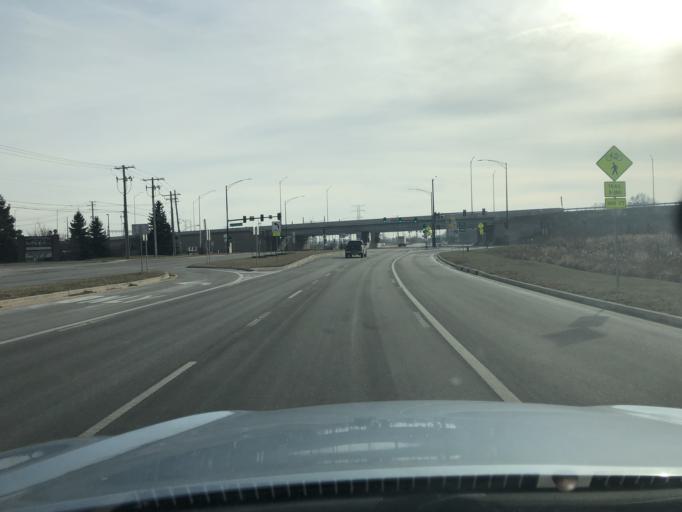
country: US
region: Illinois
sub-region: DuPage County
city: Itasca
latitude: 41.9849
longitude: -87.9991
